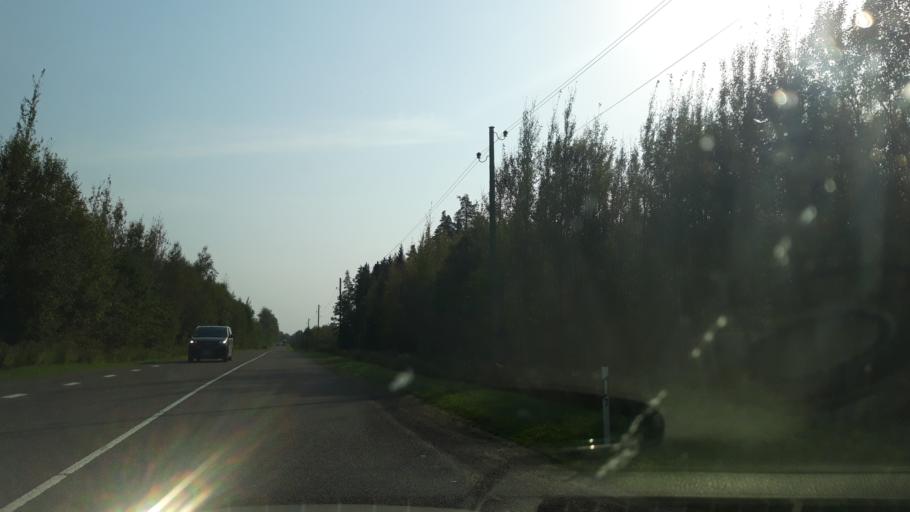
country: LV
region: Burtnieki
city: Matisi
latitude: 57.6377
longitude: 25.2536
